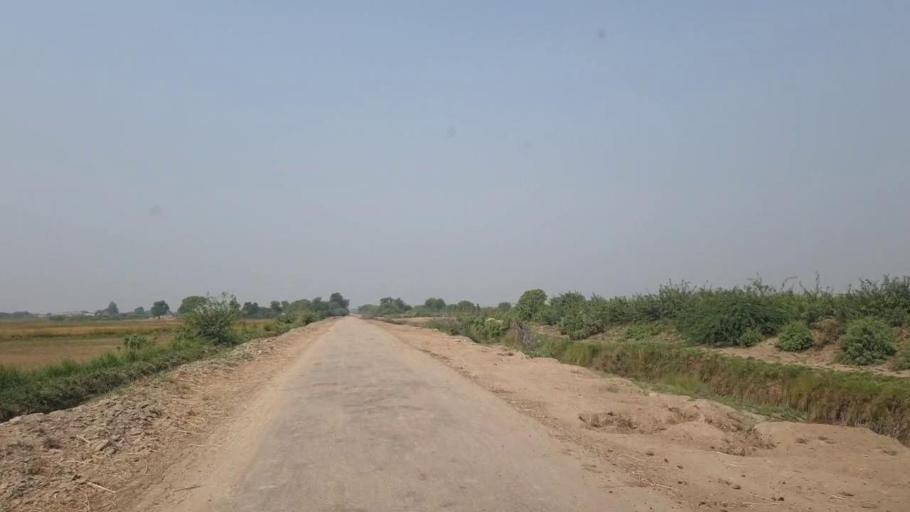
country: PK
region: Sindh
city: Matli
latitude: 25.1474
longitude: 68.7025
